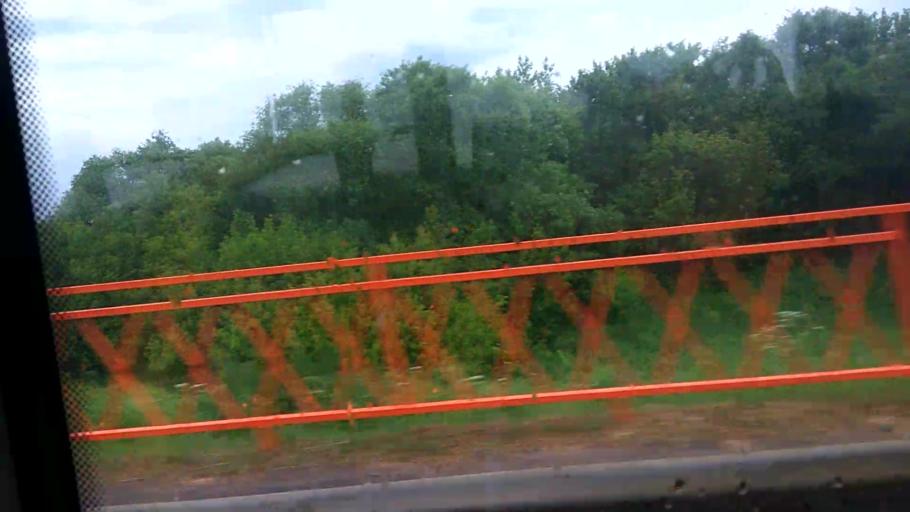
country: RU
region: Moskovskaya
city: Zaraysk
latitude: 54.7557
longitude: 38.8612
